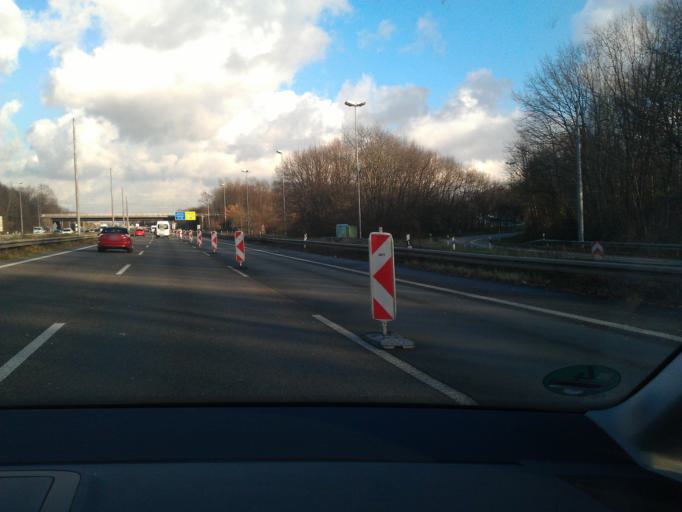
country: DE
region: North Rhine-Westphalia
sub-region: Regierungsbezirk Koln
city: Leverkusen
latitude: 51.0221
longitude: 6.9390
